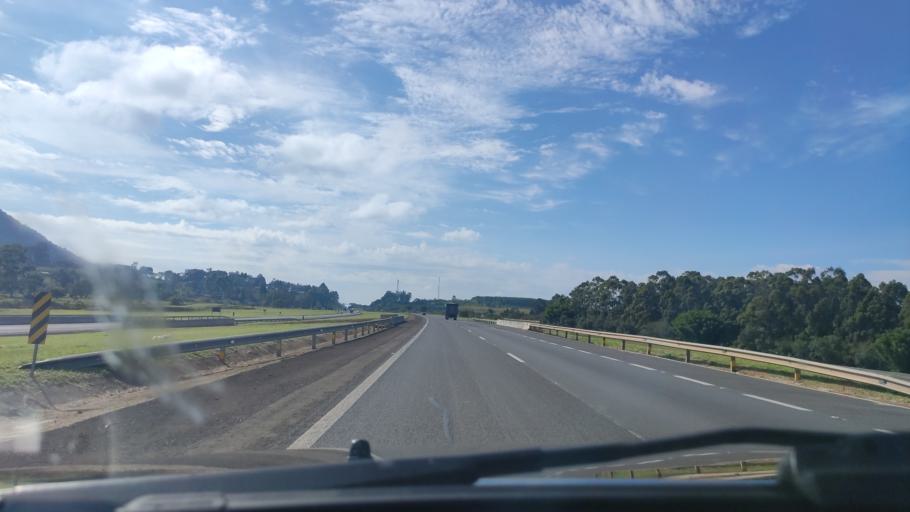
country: BR
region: Sao Paulo
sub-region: Itatinga
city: Itatinga
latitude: -23.1574
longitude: -48.3752
